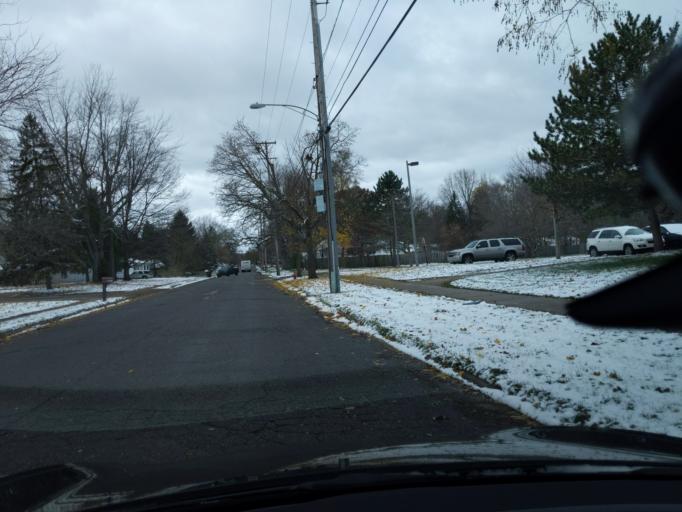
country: US
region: Michigan
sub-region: Ingham County
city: Lansing
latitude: 42.6867
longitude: -84.5863
